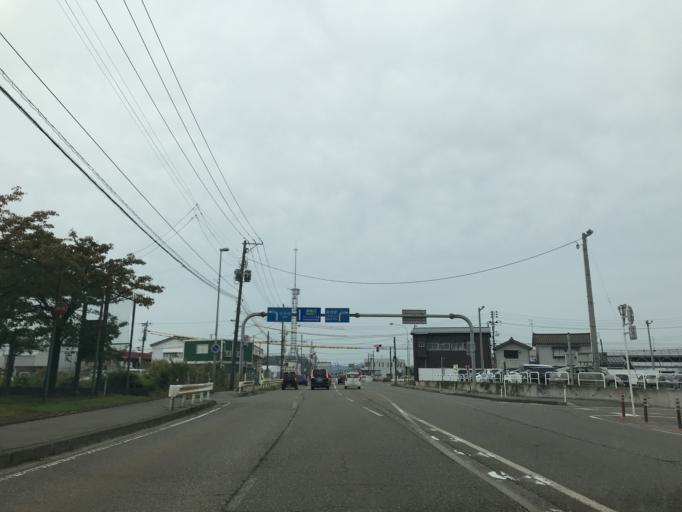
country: JP
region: Niigata
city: Nagaoka
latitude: 37.4260
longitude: 138.8402
